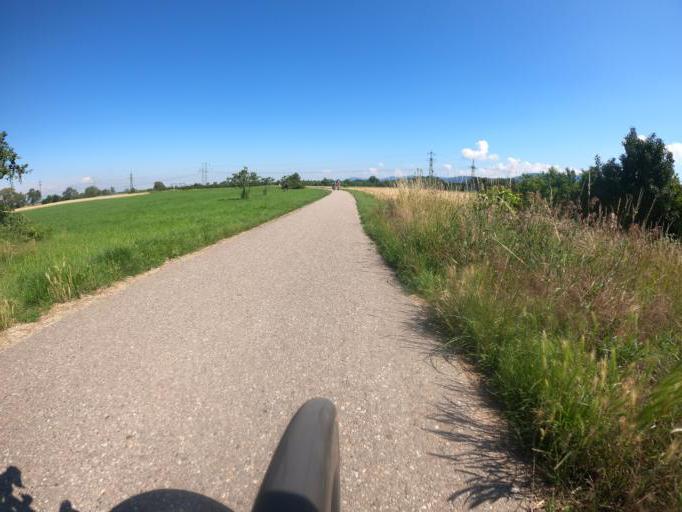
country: DE
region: Baden-Wuerttemberg
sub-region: Karlsruhe Region
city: Sandhausen
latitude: 49.3529
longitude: 8.6691
